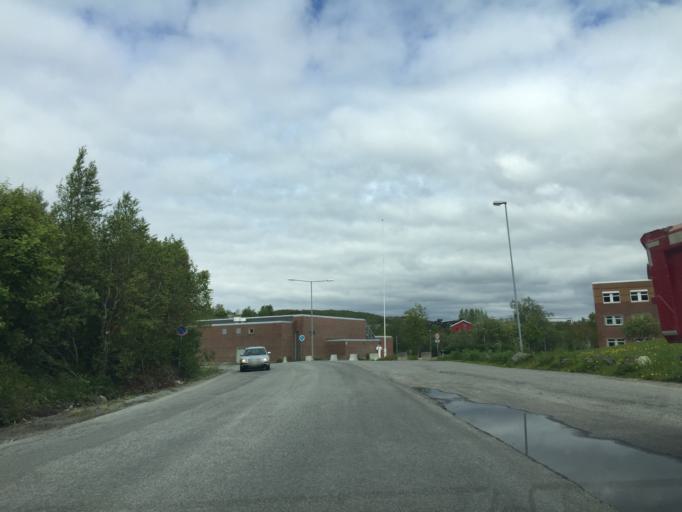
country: NO
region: Nordland
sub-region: Bodo
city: Lopsmarka
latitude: 67.2857
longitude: 14.5514
